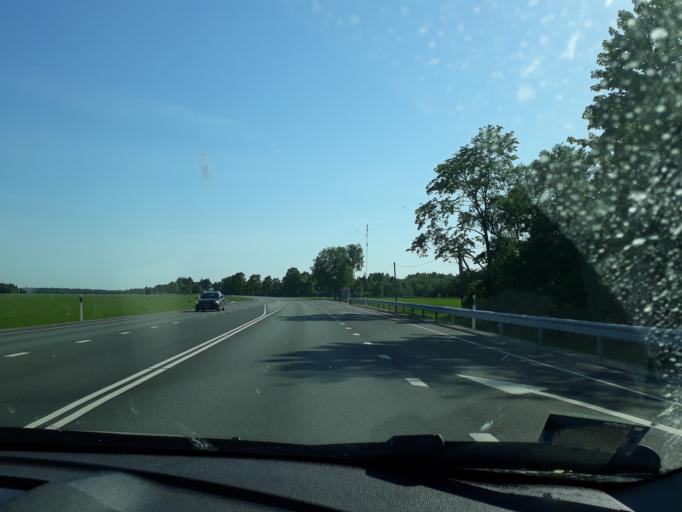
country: EE
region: Paernumaa
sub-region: Tootsi vald
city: Tootsi
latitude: 58.5527
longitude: 24.8532
